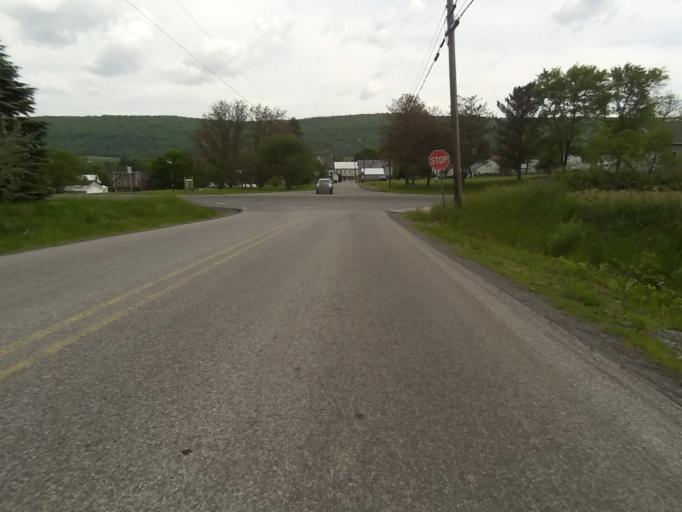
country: US
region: Pennsylvania
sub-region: Centre County
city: Zion
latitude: 40.9619
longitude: -77.6114
